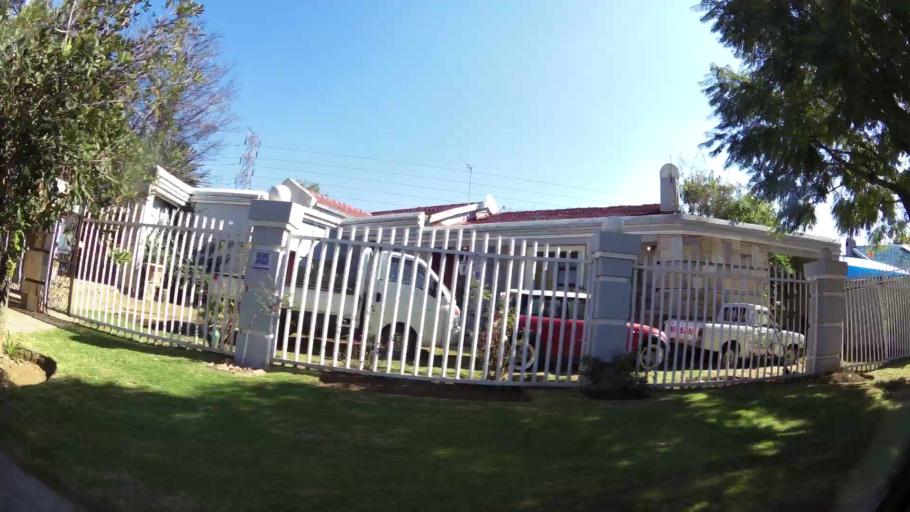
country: ZA
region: Gauteng
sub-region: City of Johannesburg Metropolitan Municipality
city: Johannesburg
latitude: -26.2727
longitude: 27.9849
